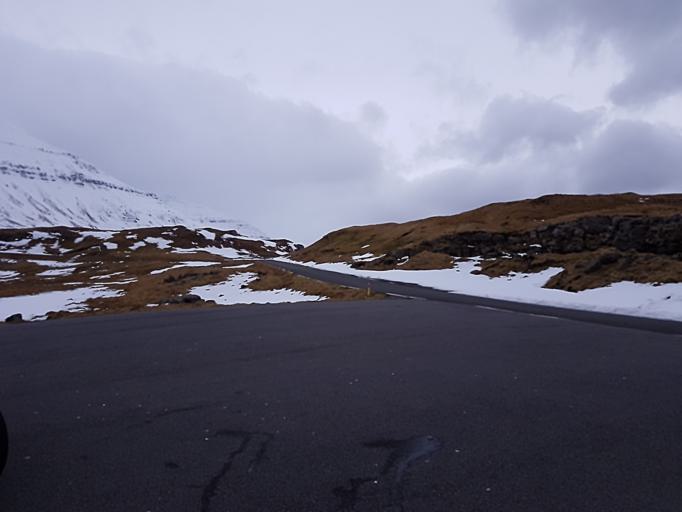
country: FO
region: Eysturoy
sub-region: Eidi
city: Eidi
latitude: 62.3038
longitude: -7.0567
